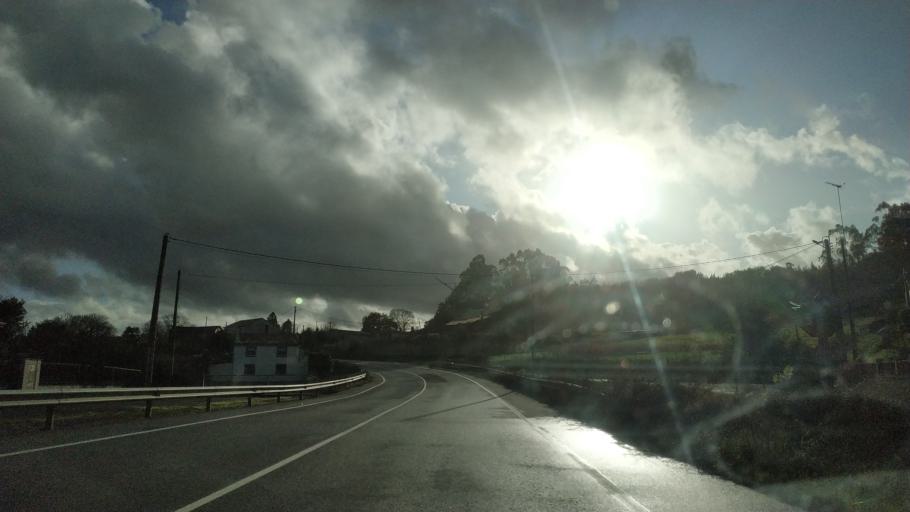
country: ES
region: Galicia
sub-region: Provincia da Coruna
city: Arzua
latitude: 42.9450
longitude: -8.1585
